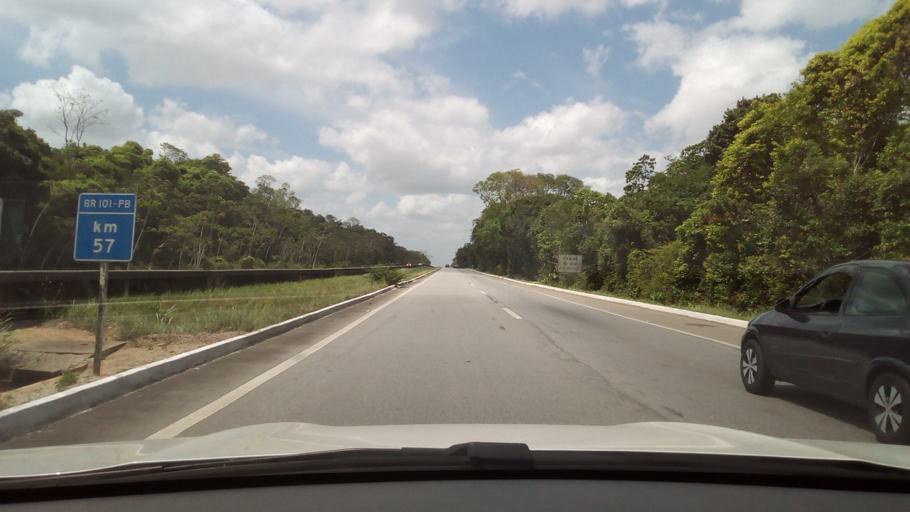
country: BR
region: Paraiba
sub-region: Mamanguape
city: Mamanguape
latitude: -6.9778
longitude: -35.0777
